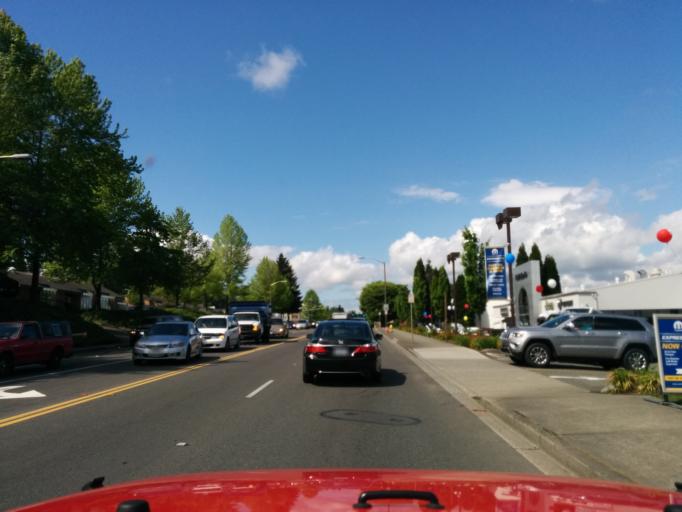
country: US
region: Washington
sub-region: King County
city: Kingsgate
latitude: 47.7113
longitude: -122.1675
